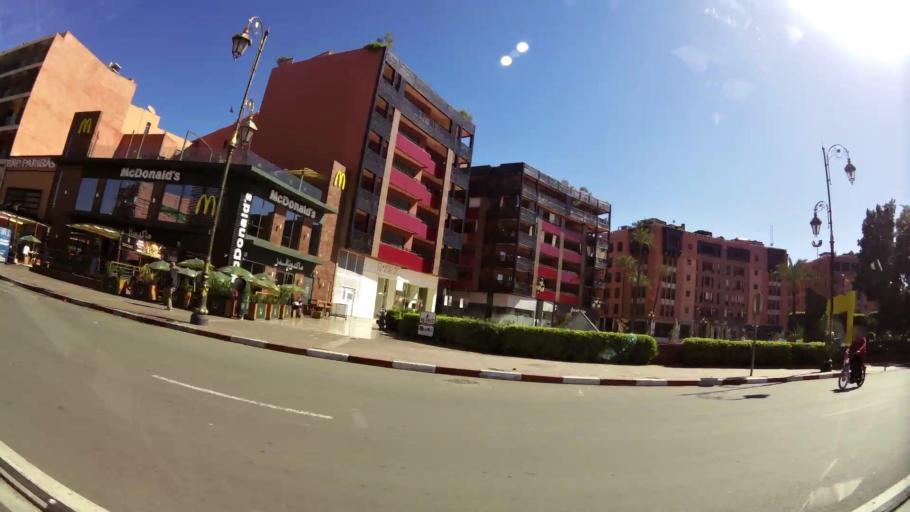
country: MA
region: Marrakech-Tensift-Al Haouz
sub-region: Marrakech
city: Marrakesh
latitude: 31.6329
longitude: -8.0089
